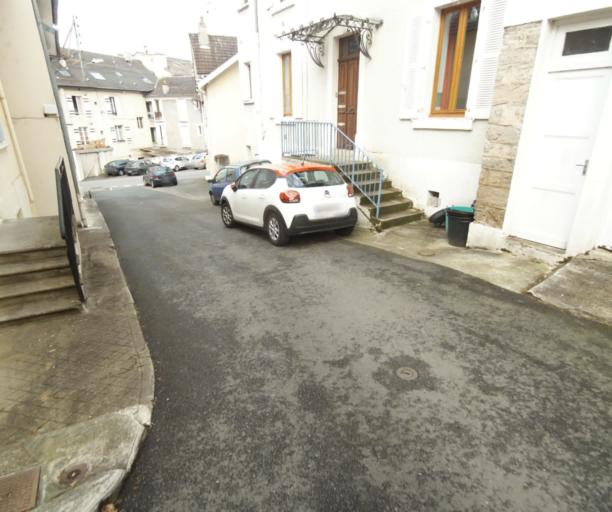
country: FR
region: Limousin
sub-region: Departement de la Correze
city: Tulle
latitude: 45.2589
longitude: 1.7514
